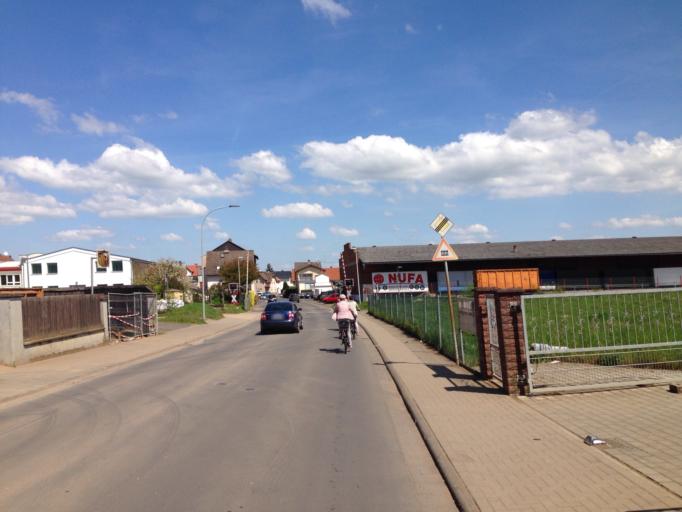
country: DE
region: Hesse
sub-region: Regierungsbezirk Giessen
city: Lich
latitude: 50.5121
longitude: 8.8270
